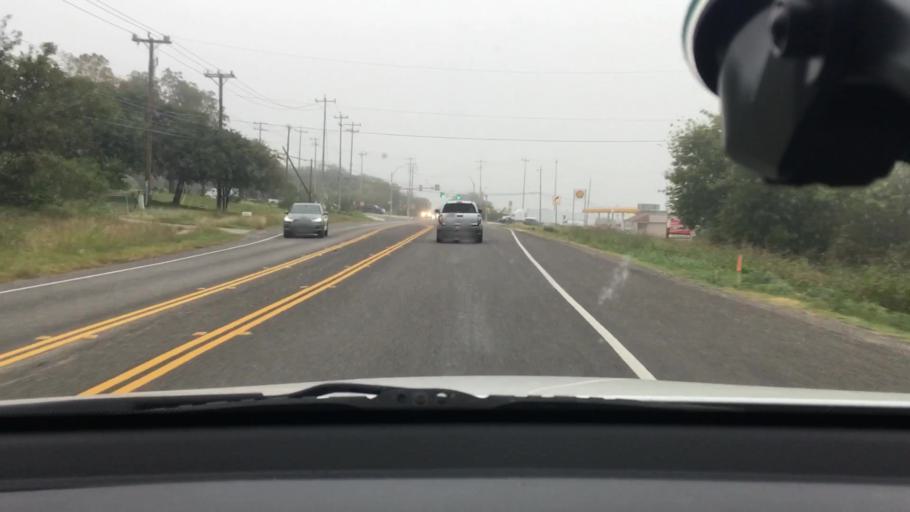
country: US
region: Texas
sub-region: Comal County
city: Garden Ridge
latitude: 29.6221
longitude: -98.2925
